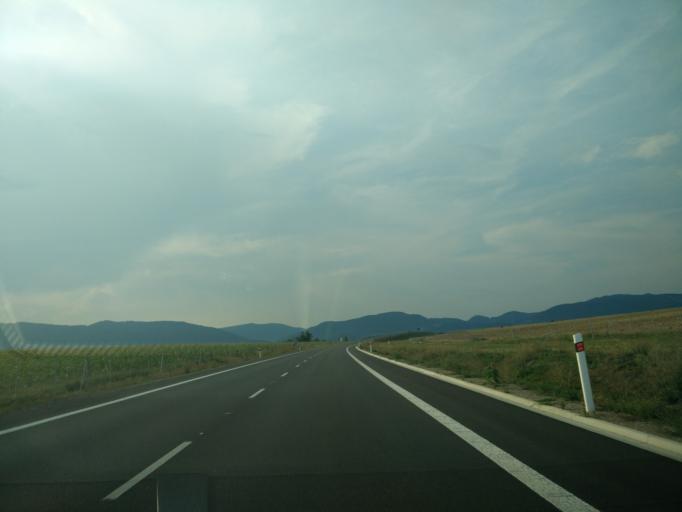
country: SK
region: Banskobystricky
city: Ziar nad Hronom
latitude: 48.6133
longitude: 18.8074
